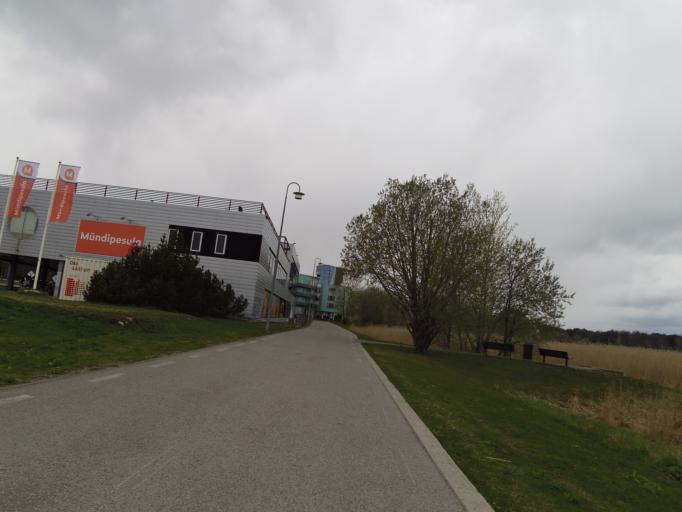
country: EE
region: Harju
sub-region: Tallinna linn
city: Tallinn
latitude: 59.4282
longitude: 24.6661
